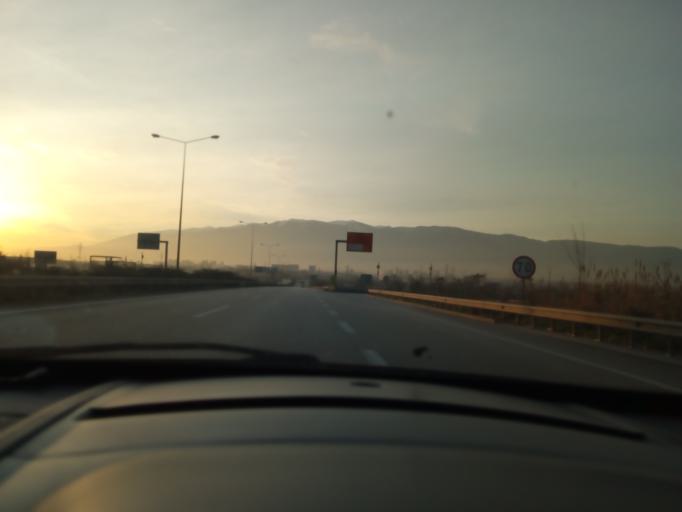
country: TR
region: Bursa
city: Demirtas
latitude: 40.2808
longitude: 29.0418
